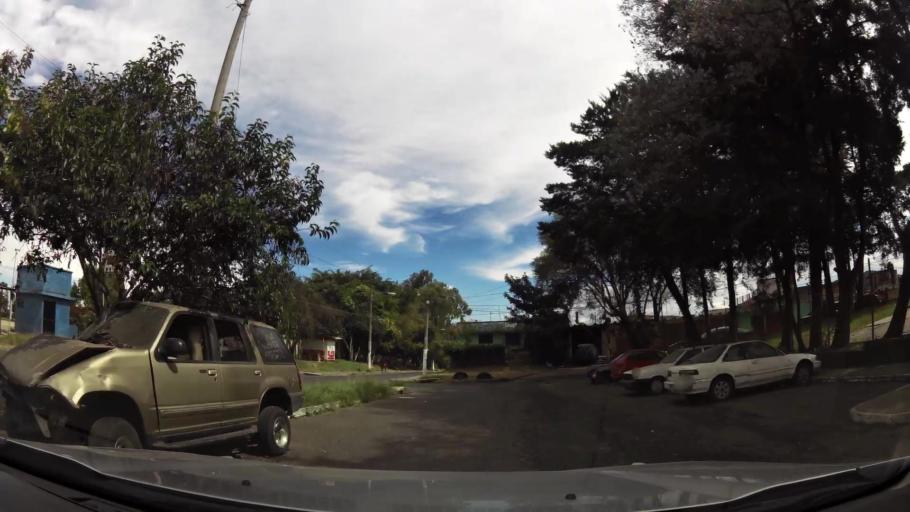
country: GT
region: Guatemala
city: Mixco
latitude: 14.6673
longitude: -90.5689
